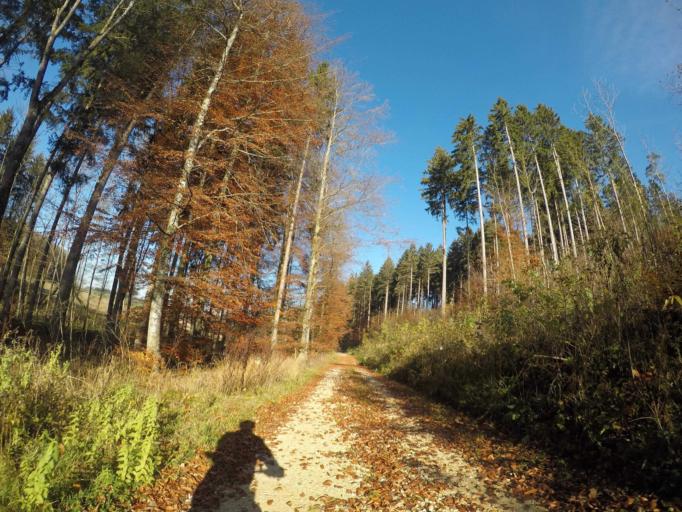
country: DE
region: Baden-Wuerttemberg
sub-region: Tuebingen Region
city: Hausen am Bussen
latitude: 48.2135
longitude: 9.6060
